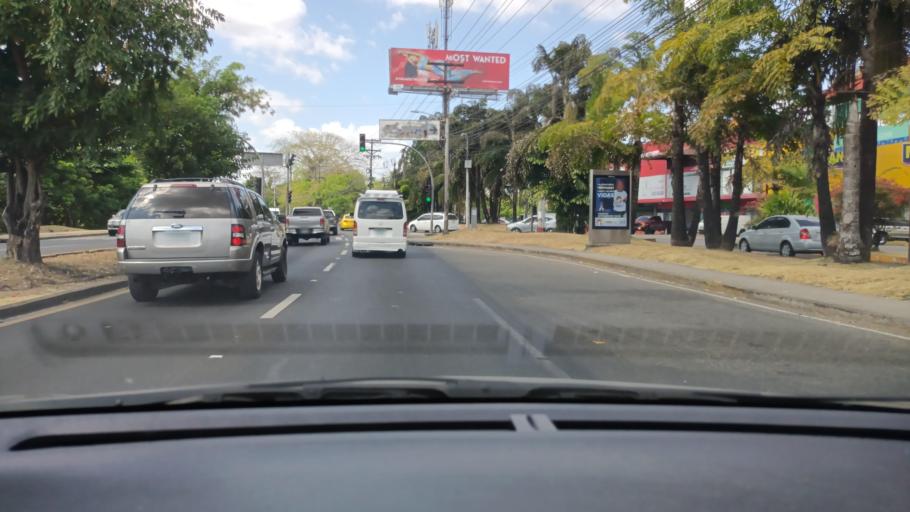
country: PA
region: Panama
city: San Miguelito
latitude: 9.0451
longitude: -79.4527
